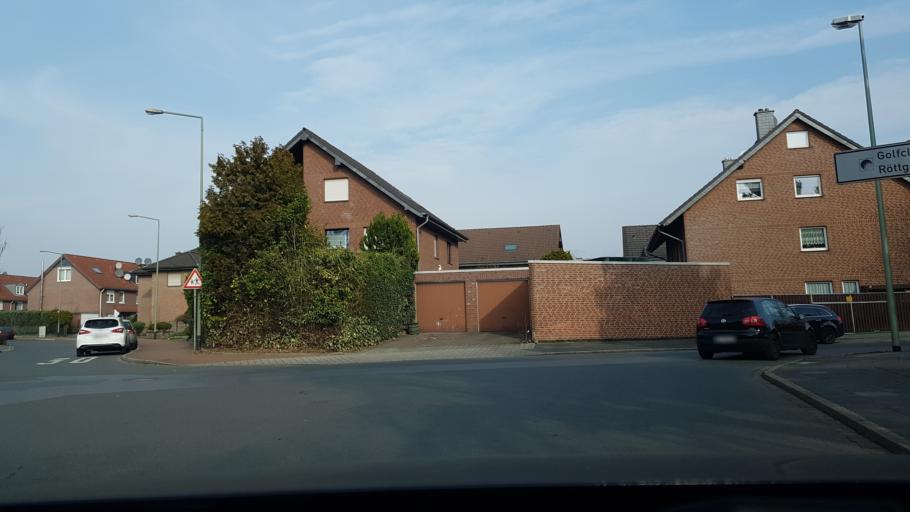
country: DE
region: North Rhine-Westphalia
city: Meiderich
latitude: 51.5104
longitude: 6.7960
